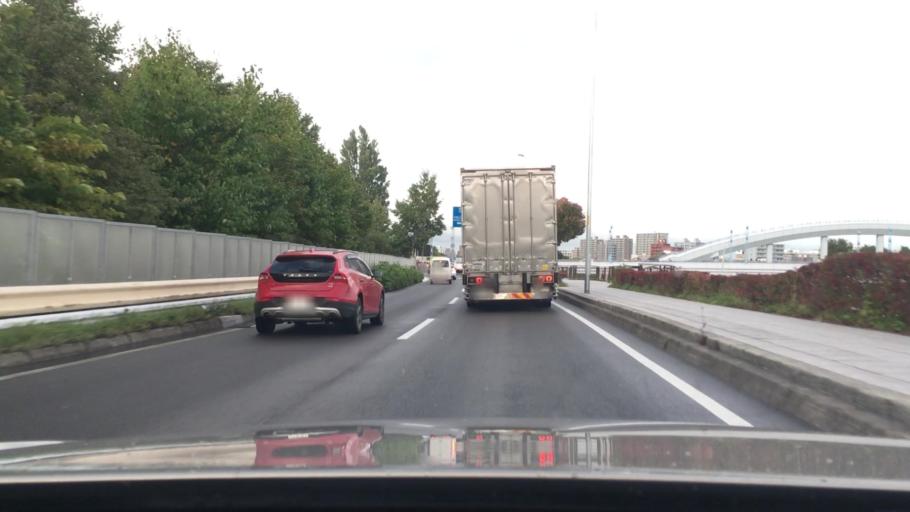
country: JP
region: Hokkaido
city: Sapporo
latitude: 43.0383
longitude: 141.3559
